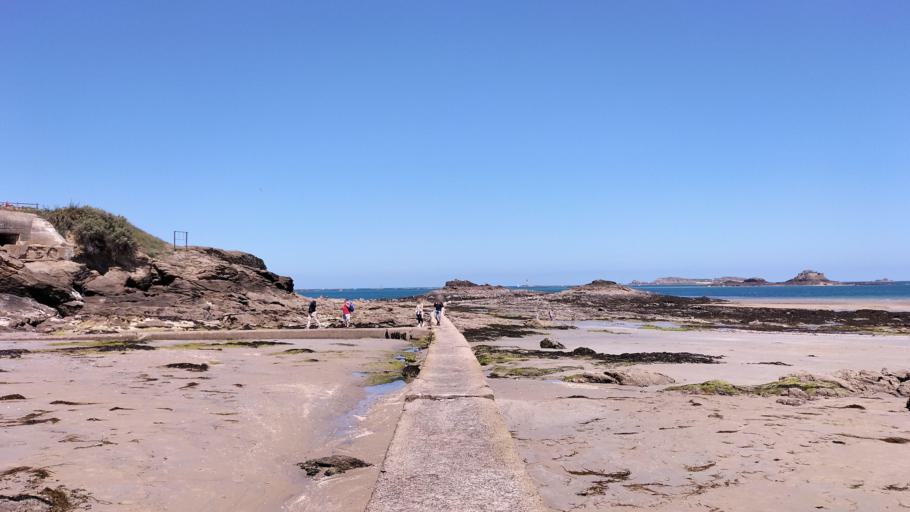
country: FR
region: Brittany
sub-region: Departement d'Ille-et-Vilaine
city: Dinard
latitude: 48.6391
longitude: -2.0723
